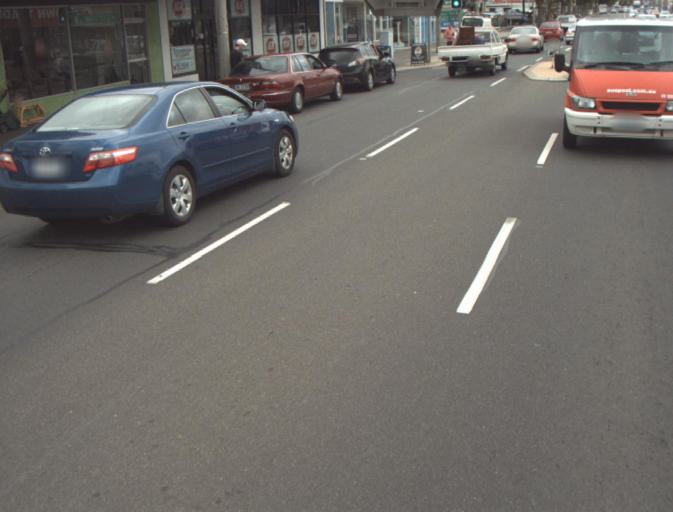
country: AU
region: Tasmania
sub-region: Launceston
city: Launceston
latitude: -41.4214
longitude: 147.1356
